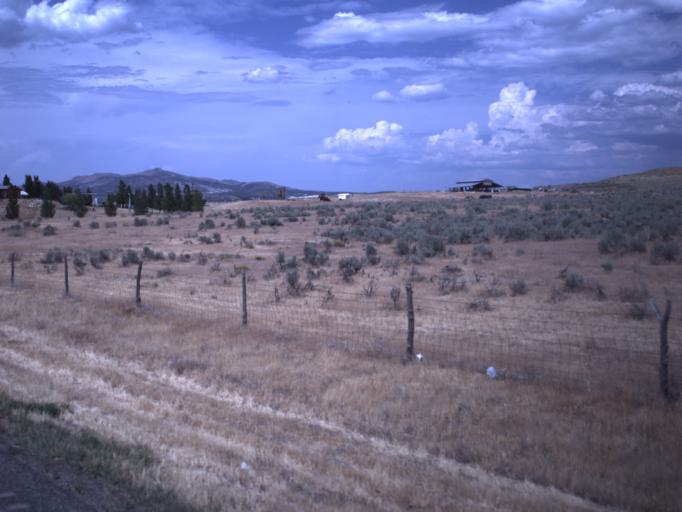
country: US
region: Utah
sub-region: Sanpete County
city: Moroni
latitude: 39.5009
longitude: -111.5660
